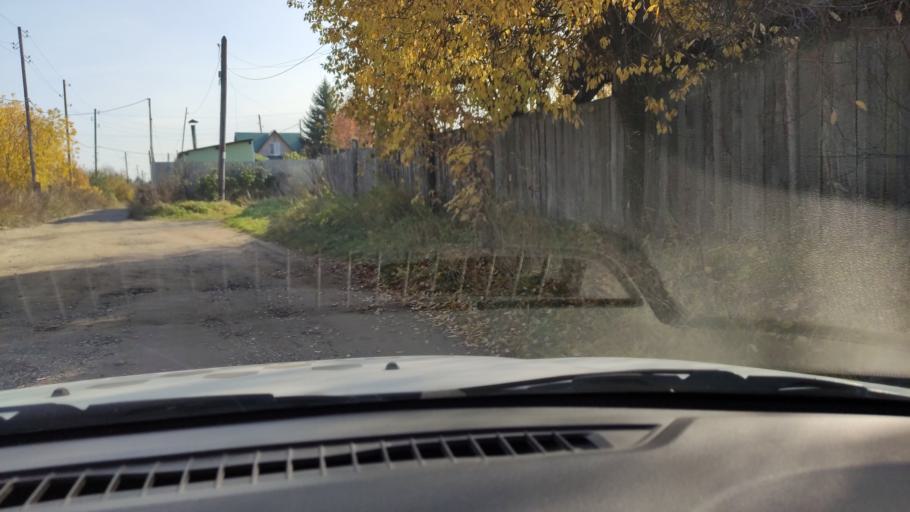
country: RU
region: Perm
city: Sylva
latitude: 58.0472
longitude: 56.7363
